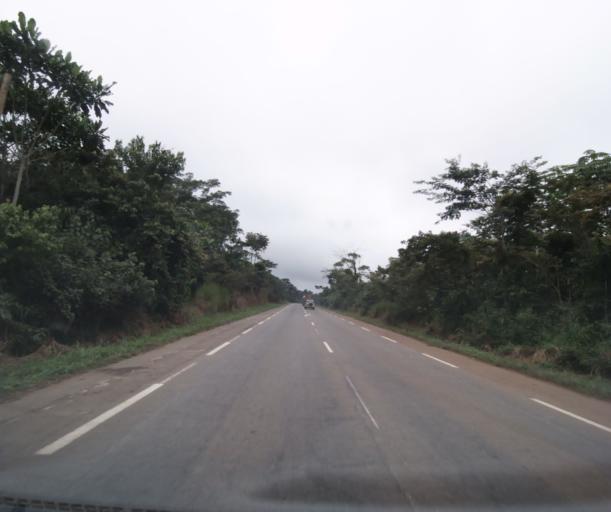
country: CM
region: Centre
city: Mbankomo
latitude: 3.7671
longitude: 11.1350
